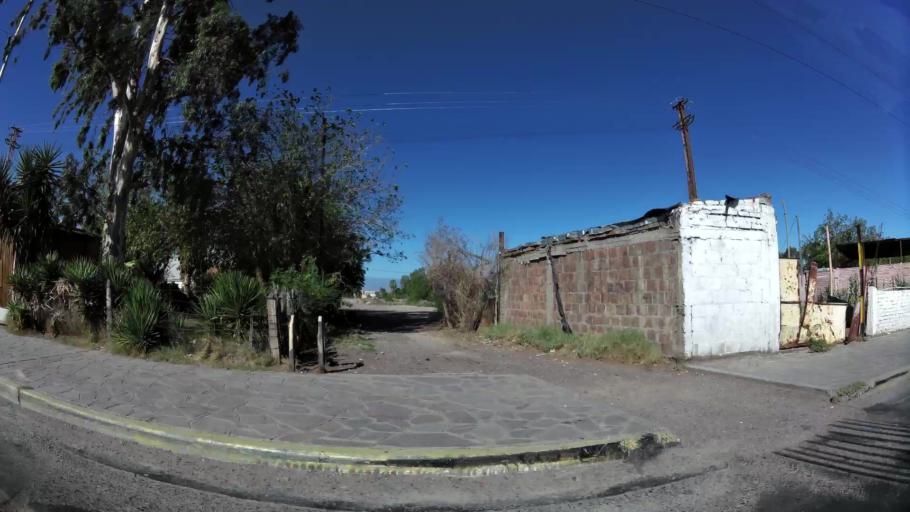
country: AR
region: San Juan
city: Villa Paula de Sarmiento
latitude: -31.5081
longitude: -68.5175
